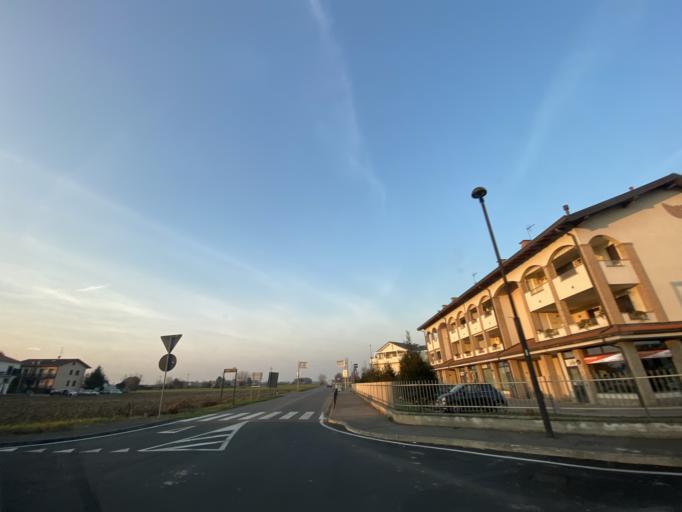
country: IT
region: Lombardy
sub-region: Citta metropolitana di Milano
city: Cesate
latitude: 45.5982
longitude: 9.0665
